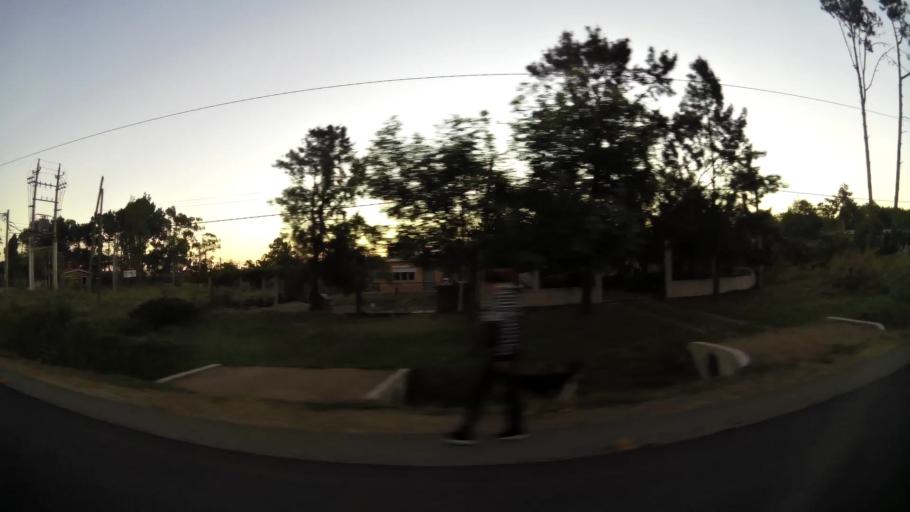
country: UY
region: Canelones
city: Barra de Carrasco
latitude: -34.8269
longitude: -55.9428
